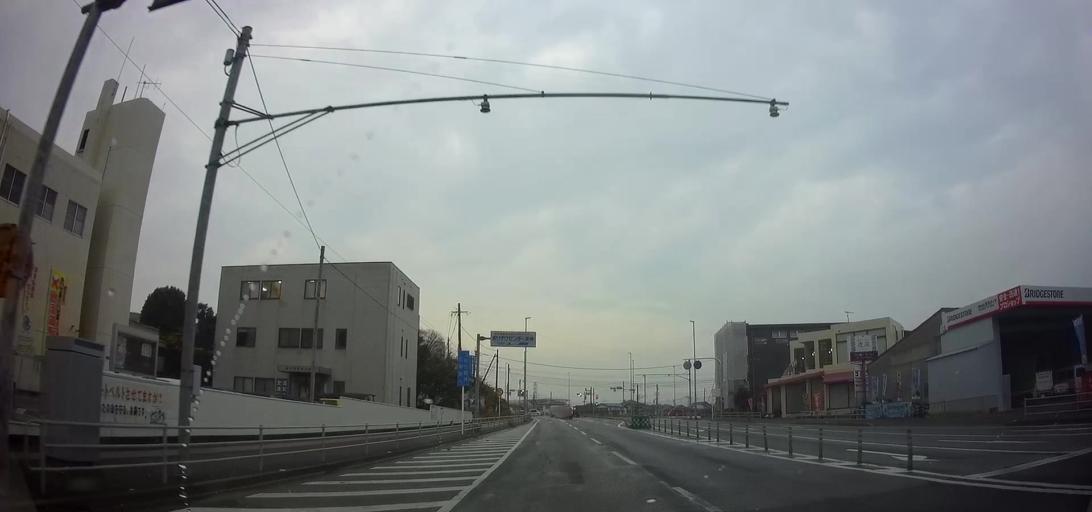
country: JP
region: Nagasaki
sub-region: Isahaya-shi
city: Isahaya
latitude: 32.8401
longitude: 130.0344
